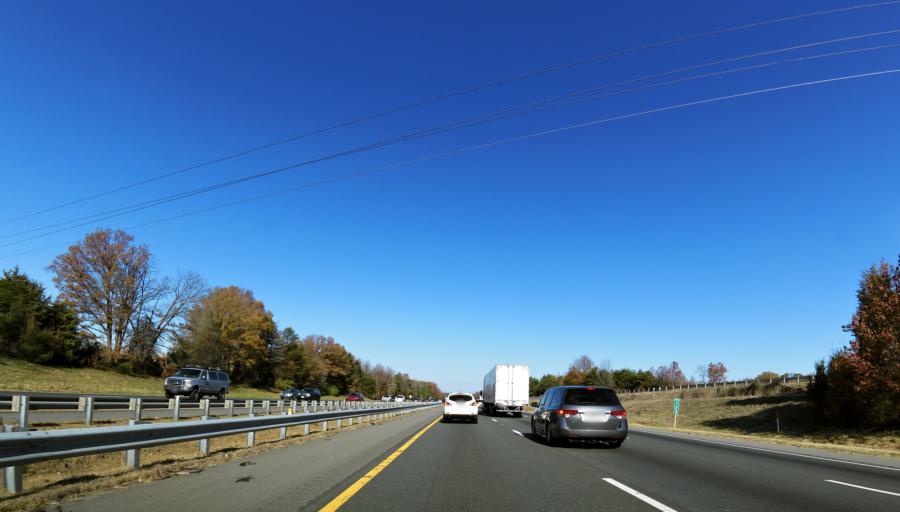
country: US
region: Virginia
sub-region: Spotsylvania County
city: Spotsylvania Courthouse
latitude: 38.1943
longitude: -77.5004
